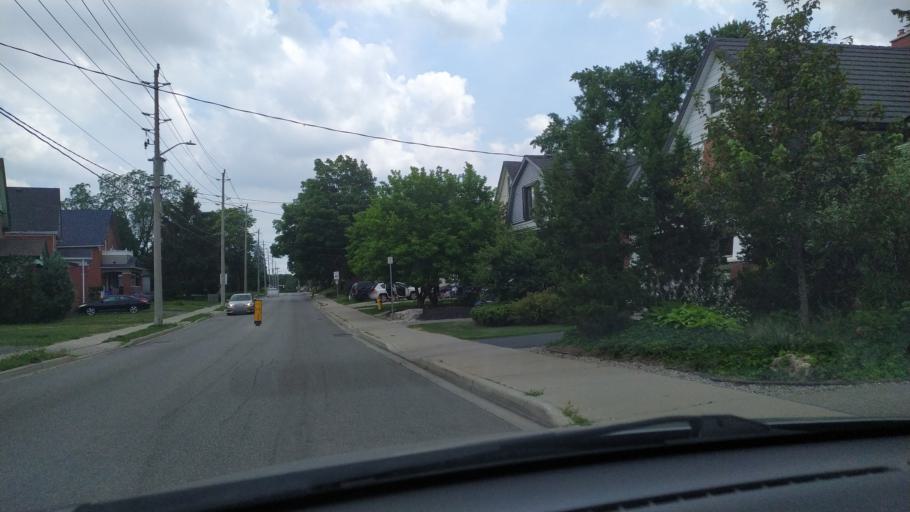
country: CA
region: Ontario
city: Waterloo
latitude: 43.4483
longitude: -80.5080
